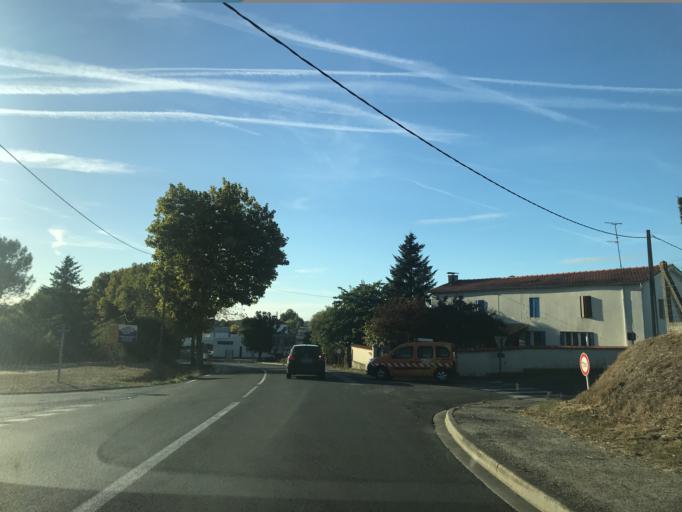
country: FR
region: Poitou-Charentes
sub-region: Departement de la Charente-Maritime
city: Montguyon
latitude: 45.2129
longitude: -0.1779
